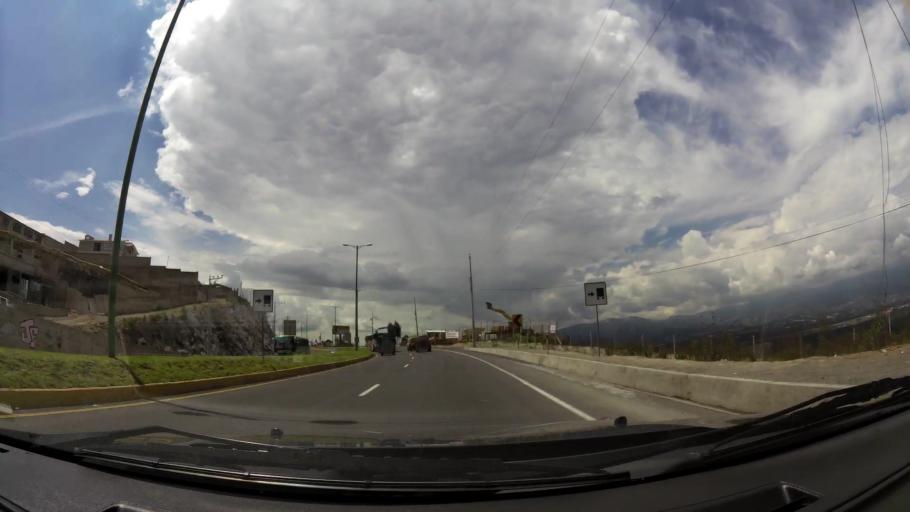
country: EC
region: Pichincha
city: Quito
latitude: -0.0977
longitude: -78.4111
